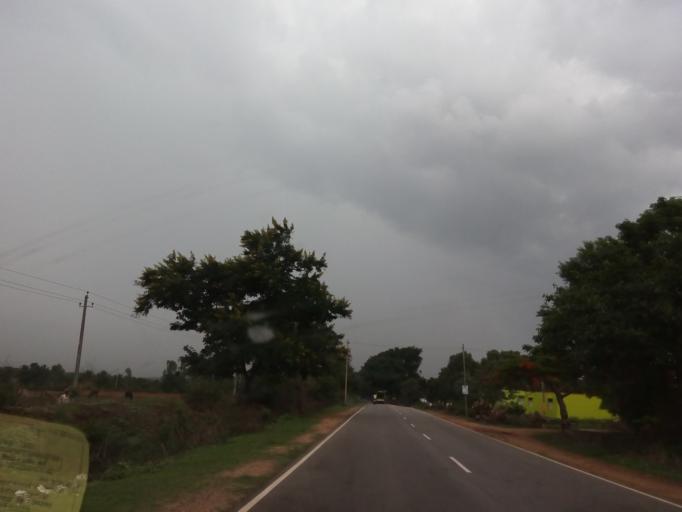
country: IN
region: Karnataka
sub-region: Hassan
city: Hassan
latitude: 13.1020
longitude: 76.0227
